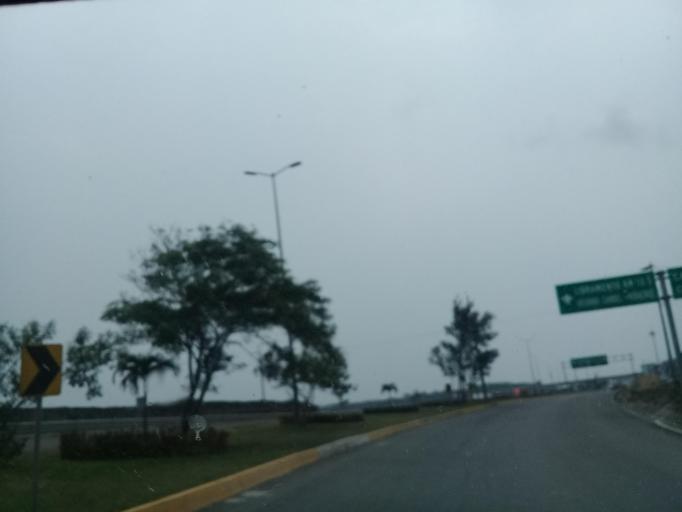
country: MX
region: Veracruz
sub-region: Veracruz
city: Colonia el Renacimiento
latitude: 19.2278
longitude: -96.2185
